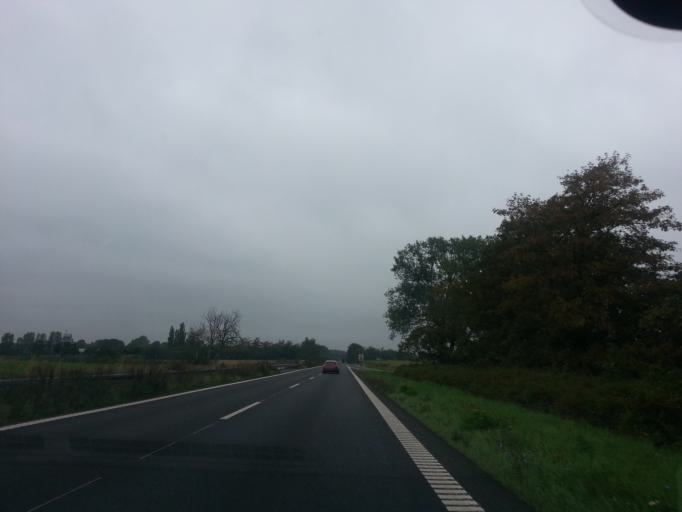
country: DK
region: Zealand
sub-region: Lolland Kommune
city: Maribo
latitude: 54.7575
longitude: 11.4620
